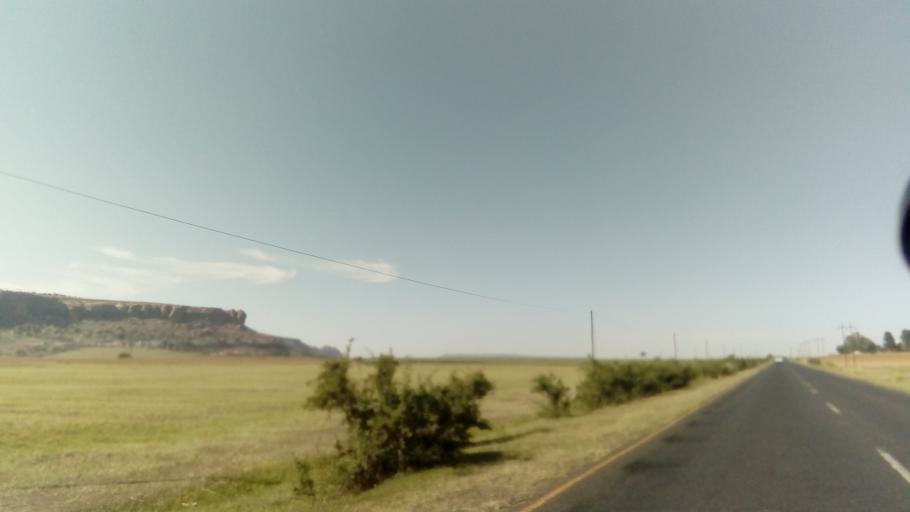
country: LS
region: Berea
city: Teyateyaneng
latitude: -29.1651
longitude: 27.6463
